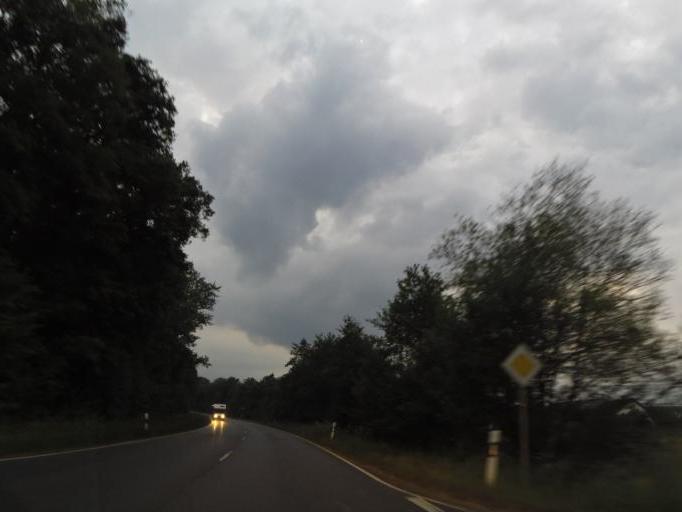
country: DE
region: Hesse
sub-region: Regierungsbezirk Darmstadt
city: Messel
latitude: 49.9284
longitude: 8.7414
